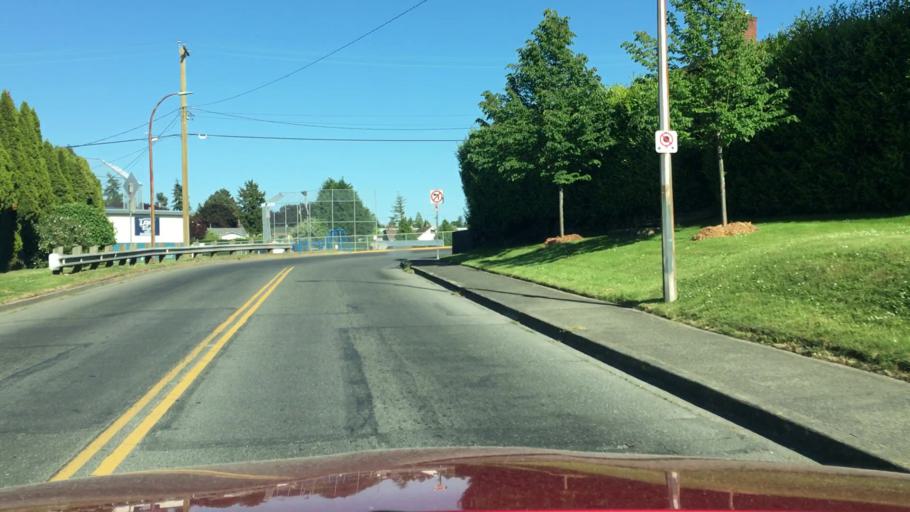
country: CA
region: British Columbia
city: Victoria
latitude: 48.4397
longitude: -123.4025
